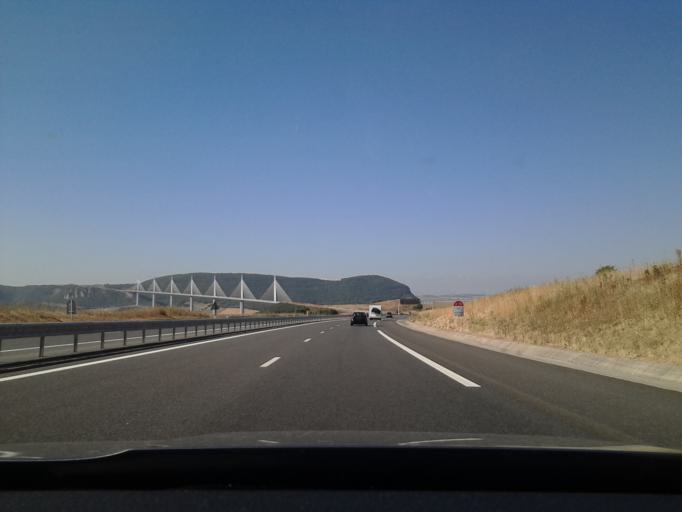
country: FR
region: Midi-Pyrenees
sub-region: Departement de l'Aveyron
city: Creissels
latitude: 44.1072
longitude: 3.0286
